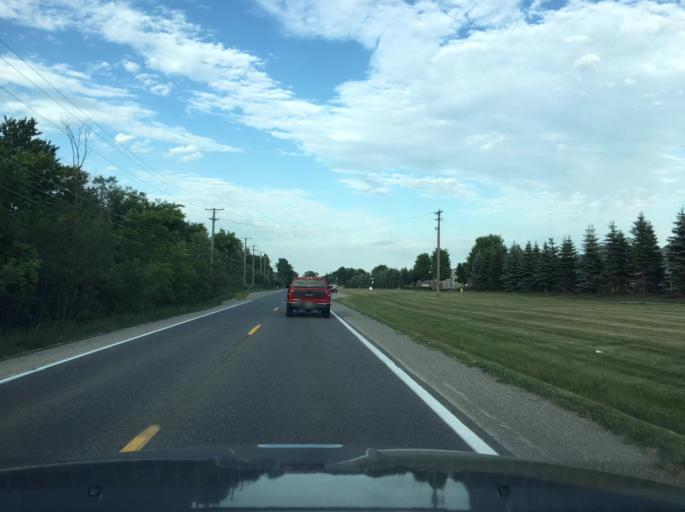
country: US
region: Michigan
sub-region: Macomb County
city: Shelby
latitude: 42.7166
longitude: -82.9345
